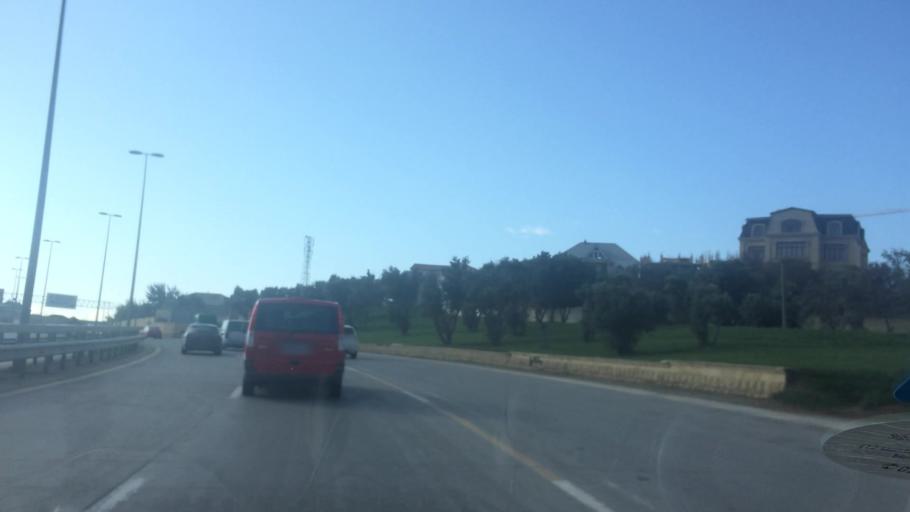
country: AZ
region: Baki
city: Qaracuxur
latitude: 40.3486
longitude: 49.9651
